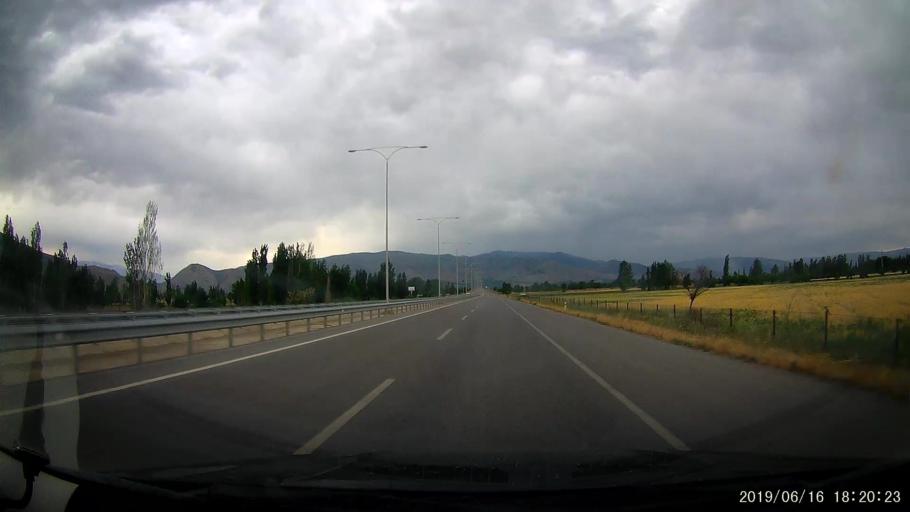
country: TR
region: Erzincan
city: Erzincan
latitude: 39.7197
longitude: 39.4703
